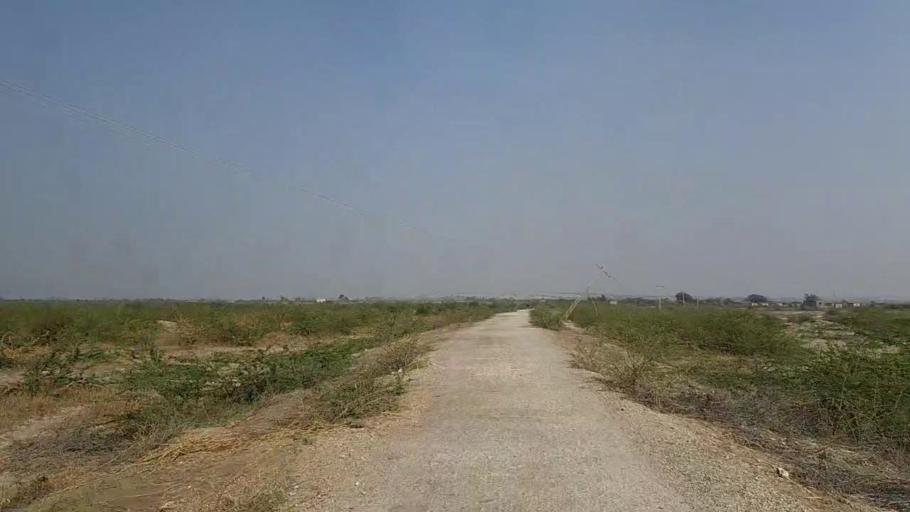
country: PK
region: Sindh
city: Naukot
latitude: 24.6680
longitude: 69.2695
